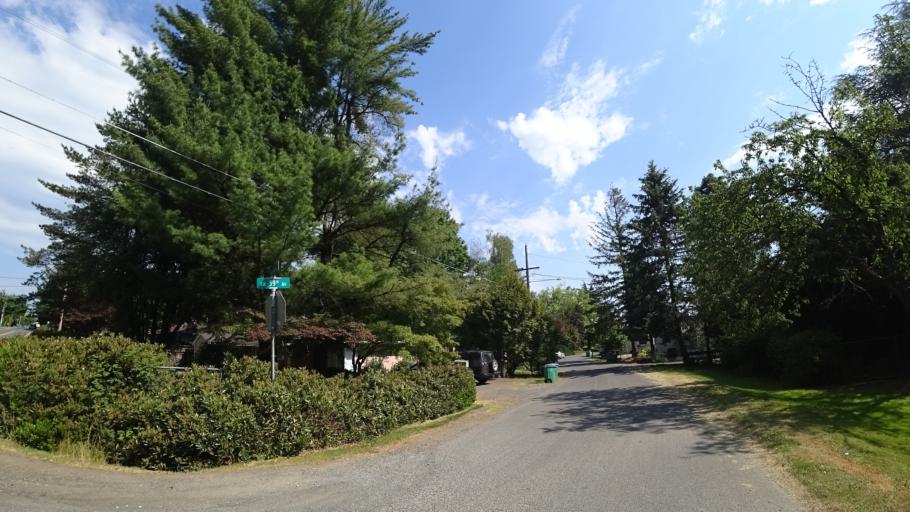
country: US
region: Oregon
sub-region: Washington County
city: Metzger
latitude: 45.4548
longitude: -122.7372
